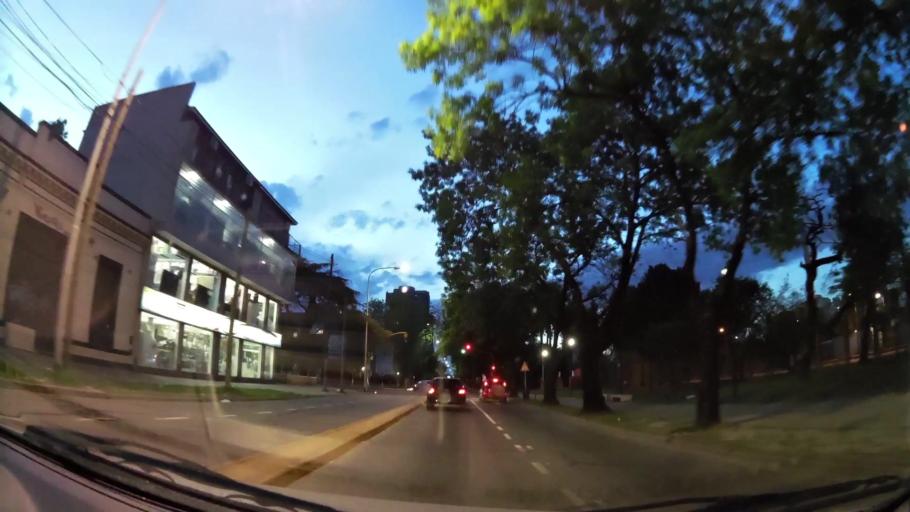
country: AR
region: Buenos Aires
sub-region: Partido de Quilmes
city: Quilmes
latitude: -34.6976
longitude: -58.3118
